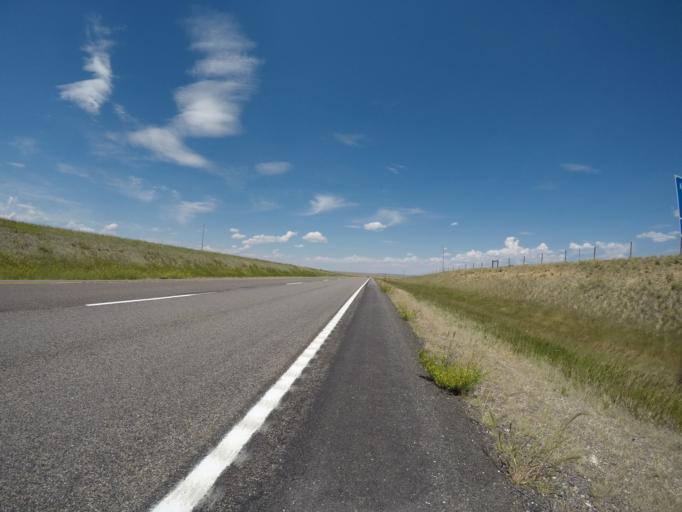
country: US
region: Wyoming
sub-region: Albany County
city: Laramie
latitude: 41.5996
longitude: -105.7185
